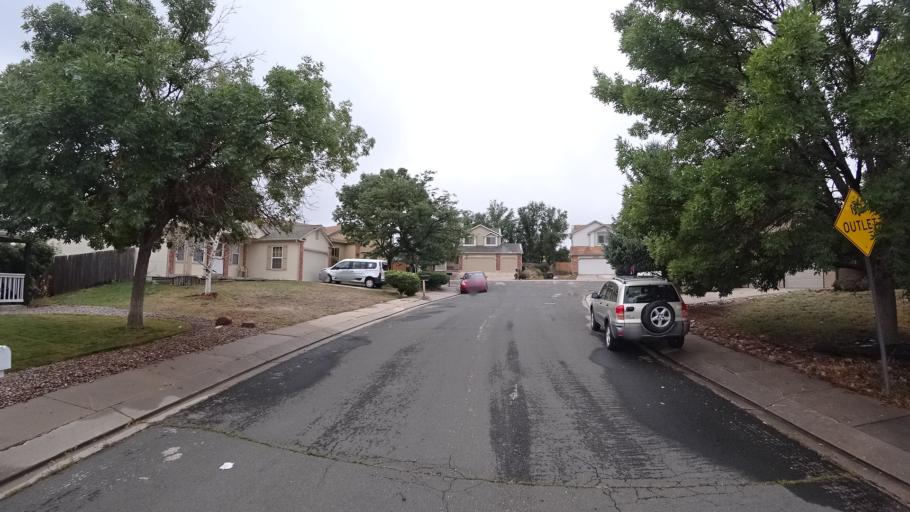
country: US
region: Colorado
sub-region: El Paso County
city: Cimarron Hills
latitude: 38.9261
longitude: -104.7635
